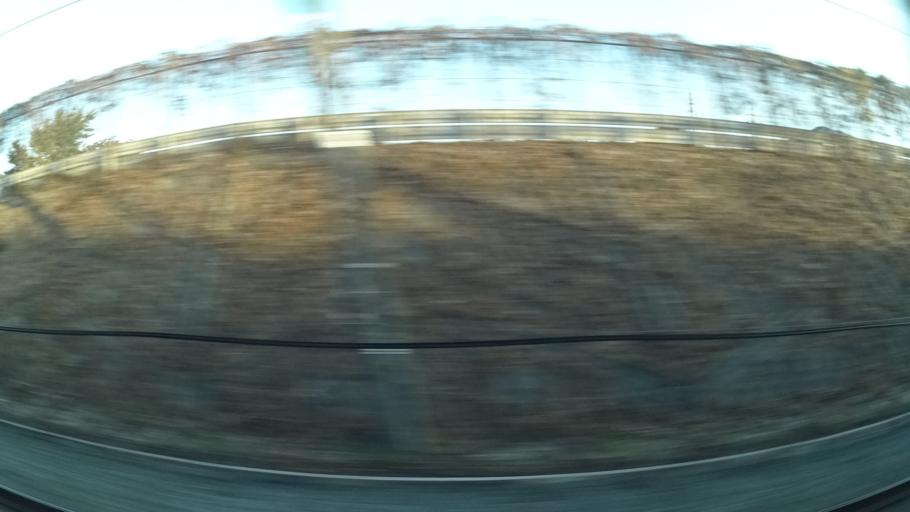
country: JP
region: Shizuoka
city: Numazu
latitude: 35.1261
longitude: 138.8406
